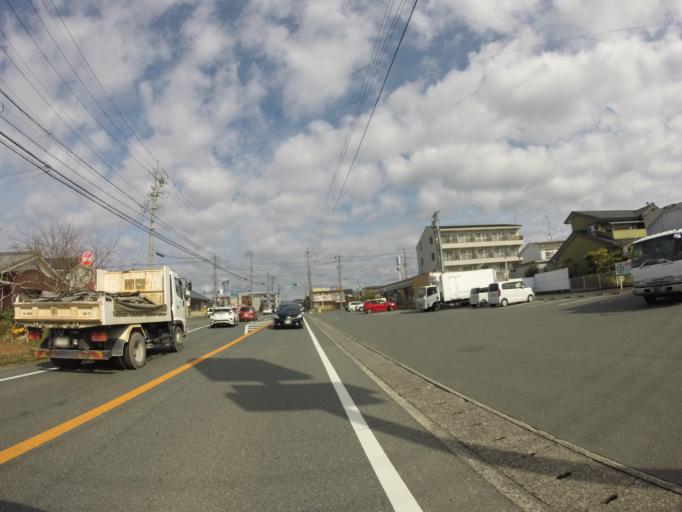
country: JP
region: Shizuoka
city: Hamakita
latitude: 34.7993
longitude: 137.6986
